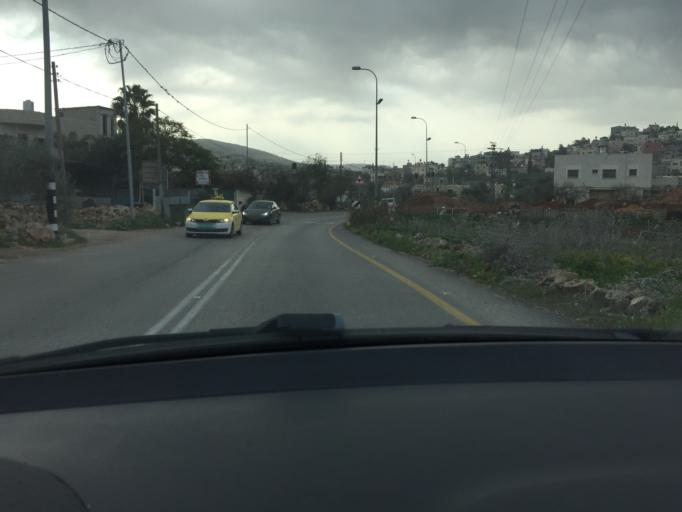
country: PS
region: West Bank
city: Al Lubban al Gharbi
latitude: 32.0392
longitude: 35.0406
